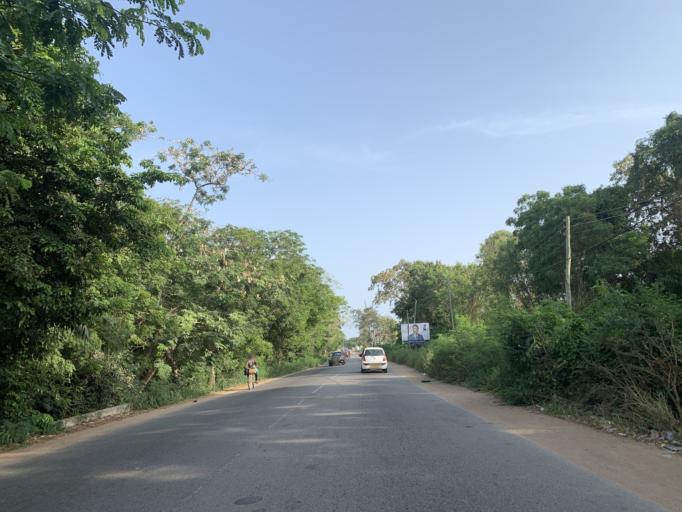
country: GH
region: Central
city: Winneba
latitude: 5.3665
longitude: -0.6366
